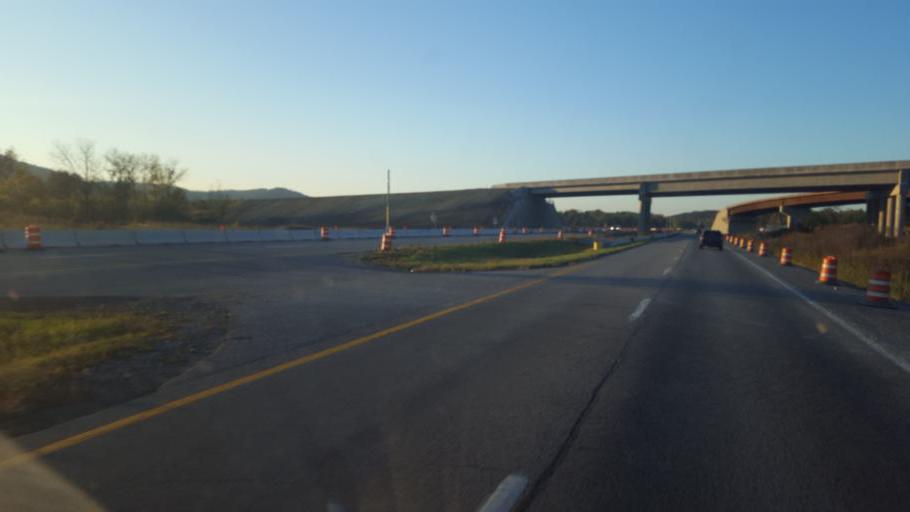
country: US
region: Ohio
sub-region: Scioto County
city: Lucasville
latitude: 38.8909
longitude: -82.9992
